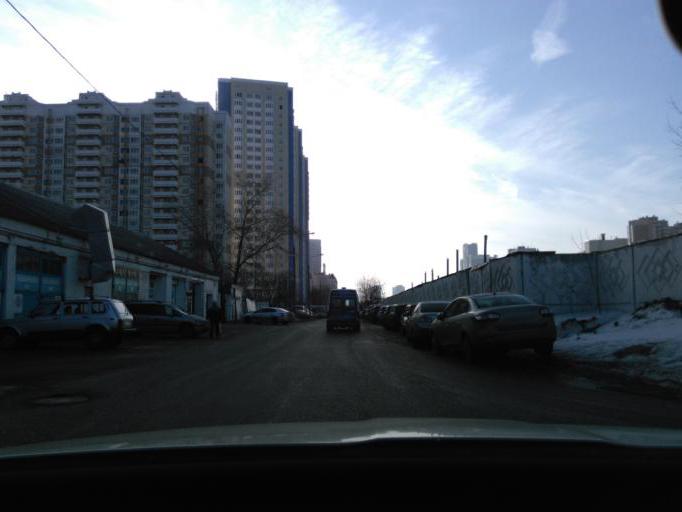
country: RU
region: Moskovskaya
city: Levoberezhnaya
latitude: 55.8724
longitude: 37.4731
